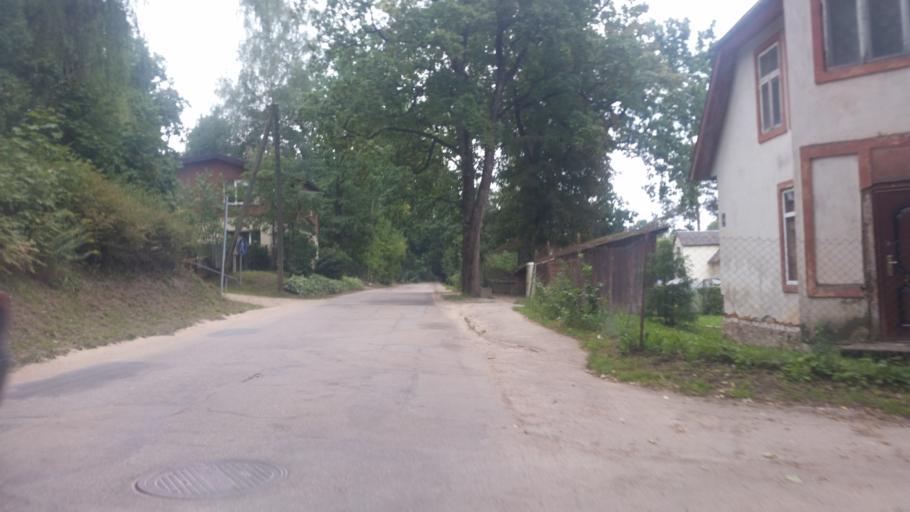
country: LV
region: Ogre
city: Ogre
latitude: 56.8105
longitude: 24.6175
